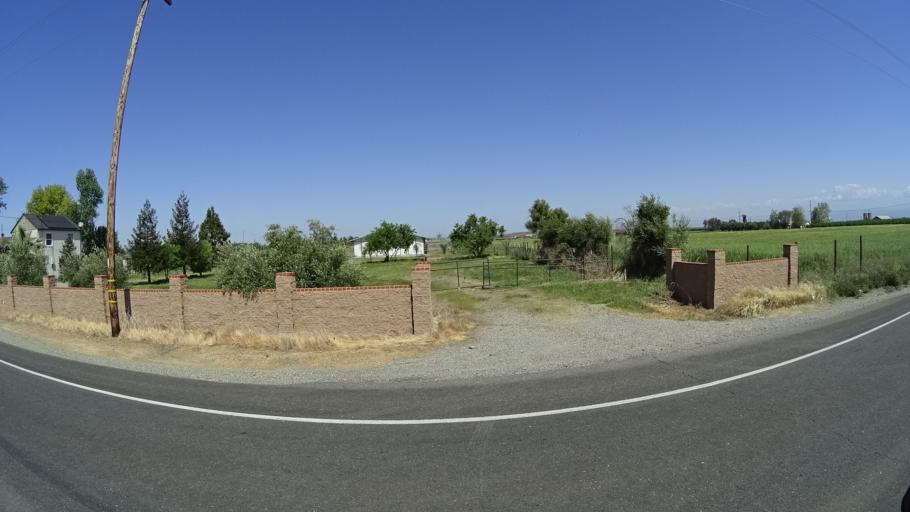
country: US
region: California
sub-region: Glenn County
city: Orland
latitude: 39.7685
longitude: -122.1435
